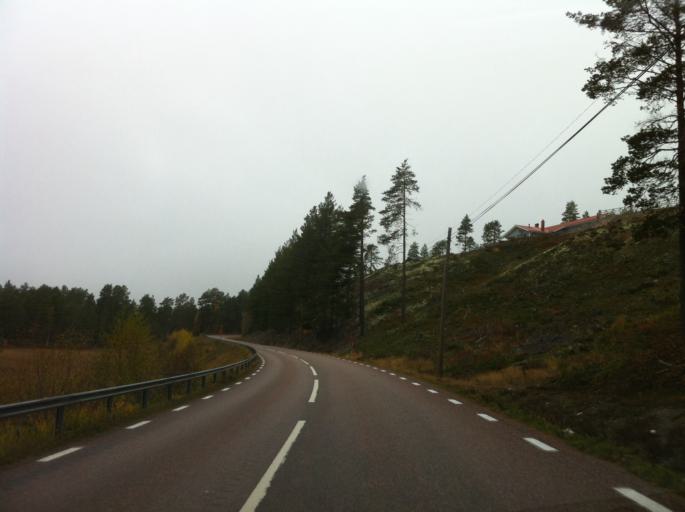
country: NO
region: Hedmark
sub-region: Trysil
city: Innbygda
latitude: 61.8552
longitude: 12.7389
